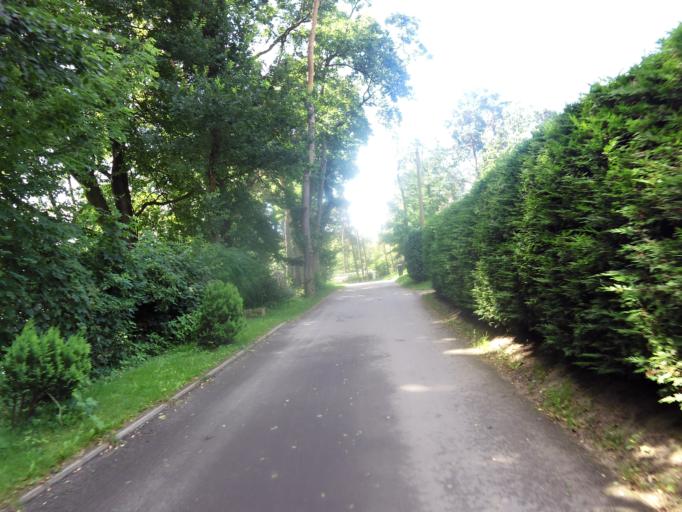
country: DE
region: Brandenburg
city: Lychen
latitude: 53.2065
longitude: 13.2758
